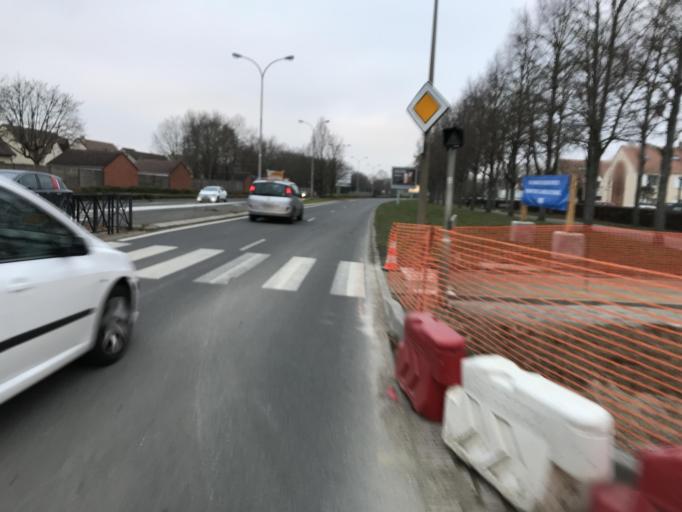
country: FR
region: Ile-de-France
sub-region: Departement des Yvelines
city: Voisins-le-Bretonneux
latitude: 48.7549
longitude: 2.0599
